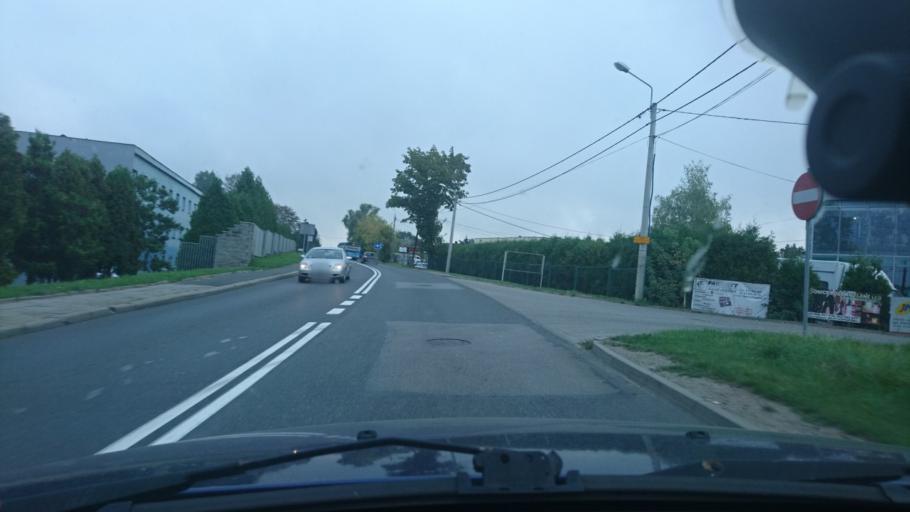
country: PL
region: Silesian Voivodeship
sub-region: Bielsko-Biala
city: Bielsko-Biala
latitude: 49.8587
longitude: 19.0346
